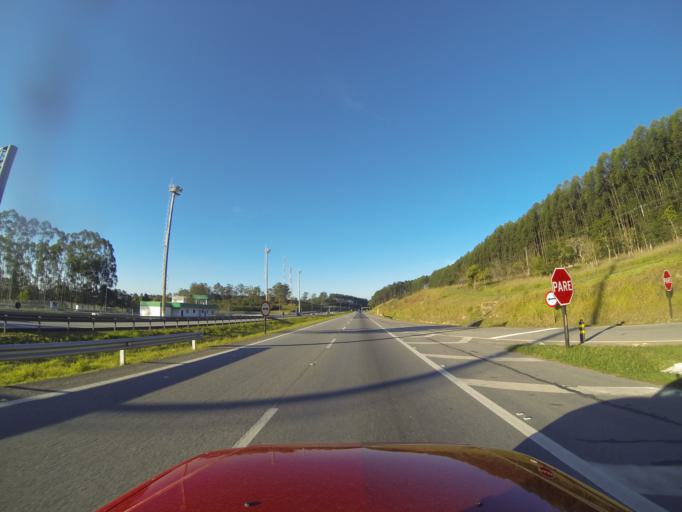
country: BR
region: Sao Paulo
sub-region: Sao Jose Dos Campos
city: Sao Jose dos Campos
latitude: -23.2818
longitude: -45.8584
